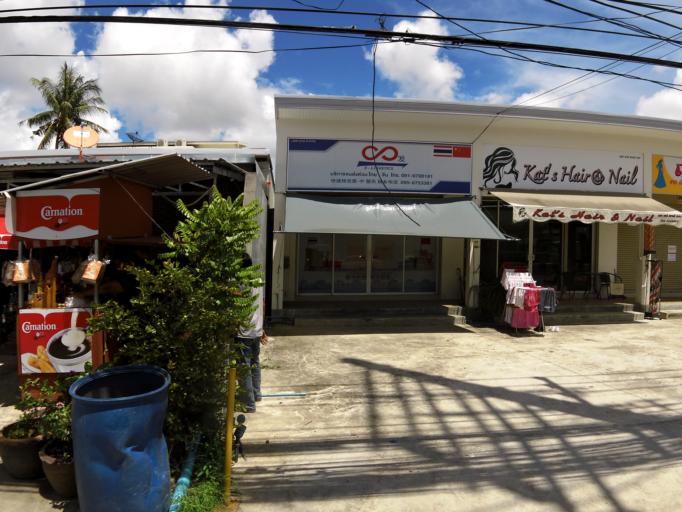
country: TH
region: Phuket
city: Mueang Phuket
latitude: 7.8803
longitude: 98.3638
